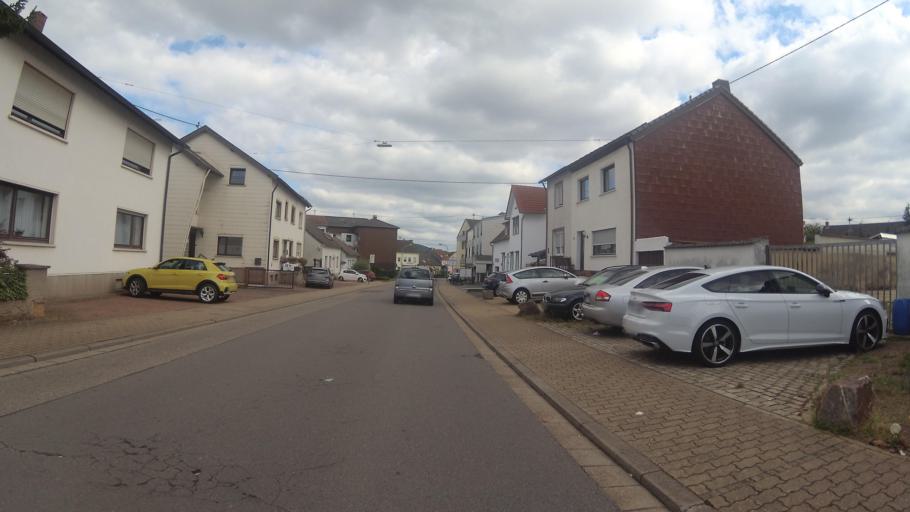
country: DE
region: Saarland
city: Bous
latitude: 49.2589
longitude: 6.8100
